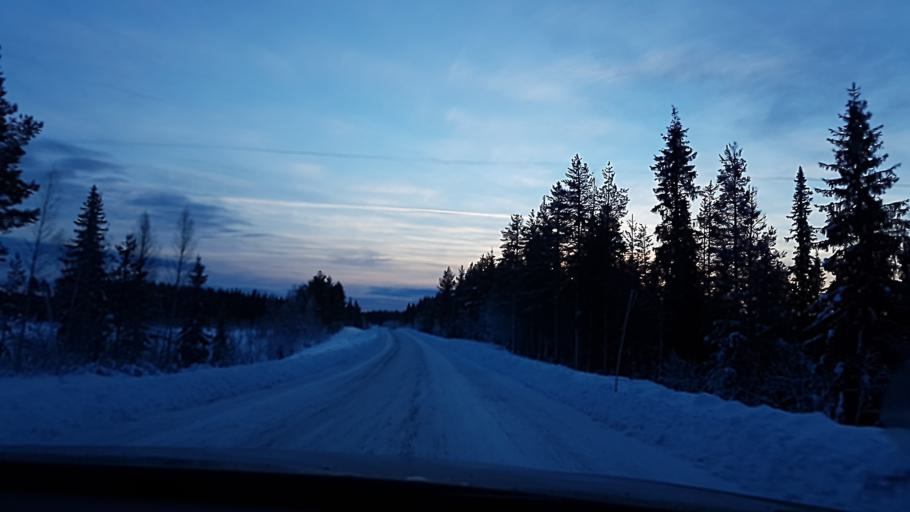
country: SE
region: Norrbotten
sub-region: Jokkmokks Kommun
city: Jokkmokk
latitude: 66.1196
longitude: 20.0330
